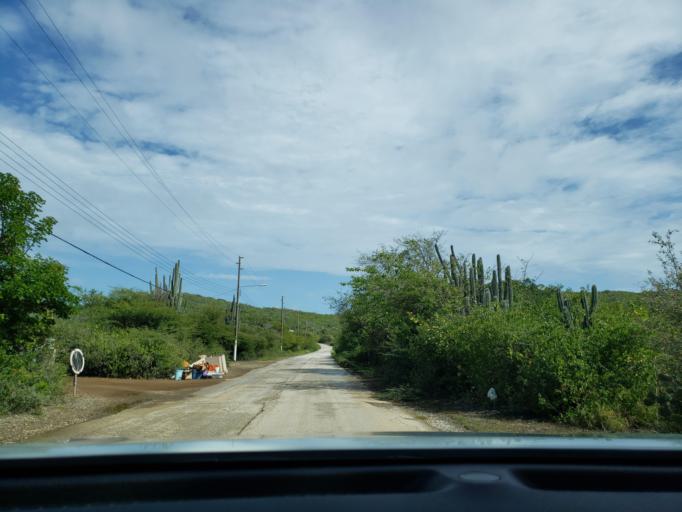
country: CW
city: Barber
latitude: 12.3055
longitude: -69.0909
